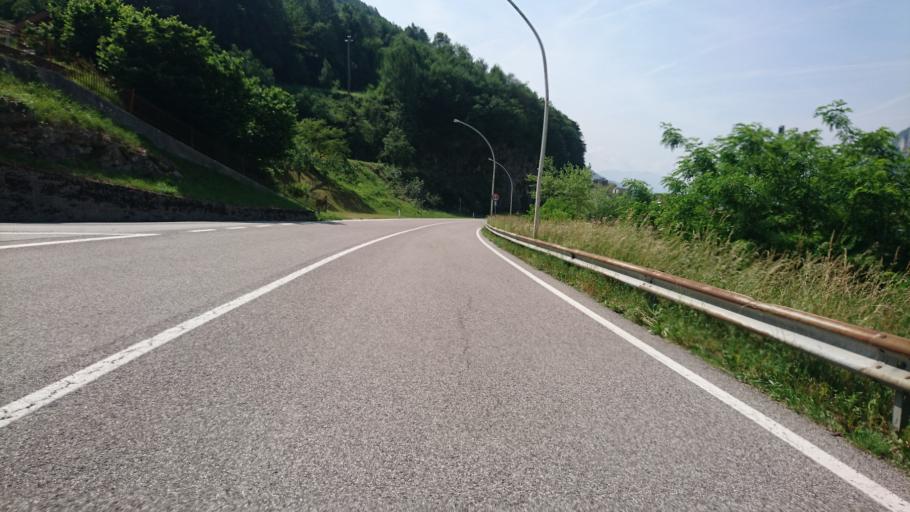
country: IT
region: Veneto
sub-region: Provincia di Belluno
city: Castello Lavazzo
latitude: 46.2744
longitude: 12.3090
